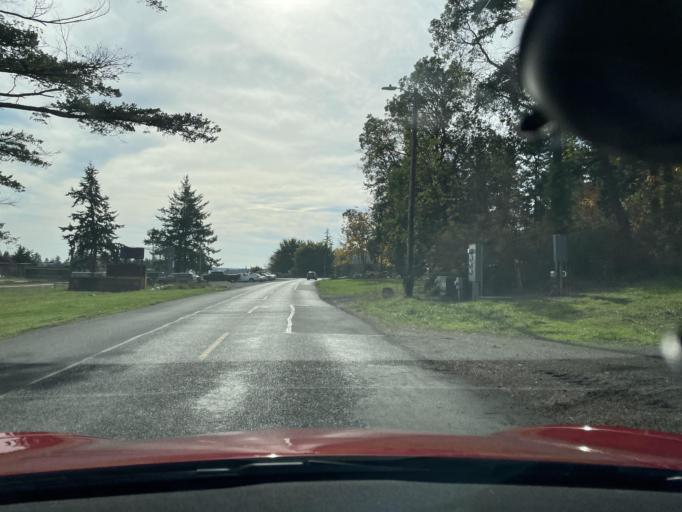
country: US
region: Washington
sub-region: San Juan County
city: Friday Harbor
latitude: 48.5326
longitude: -123.0269
